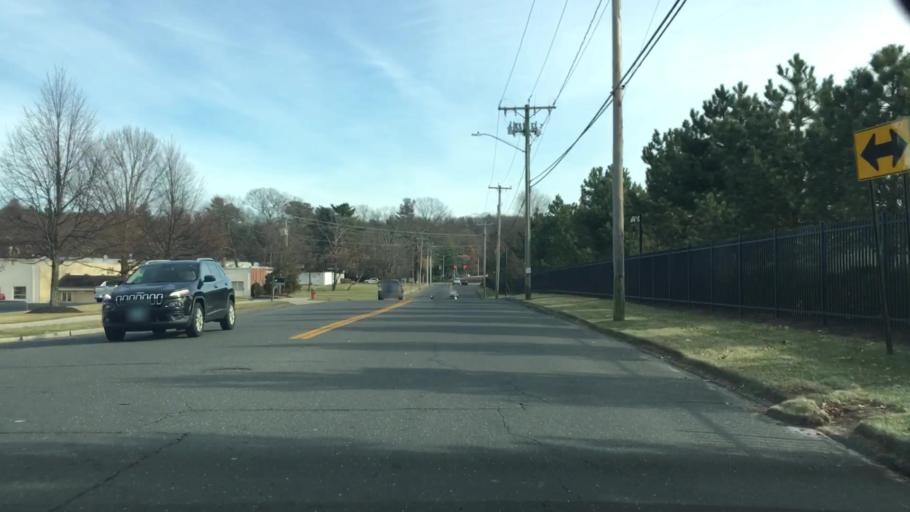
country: US
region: Connecticut
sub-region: Hartford County
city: Bristol
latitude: 41.6515
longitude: -72.9048
